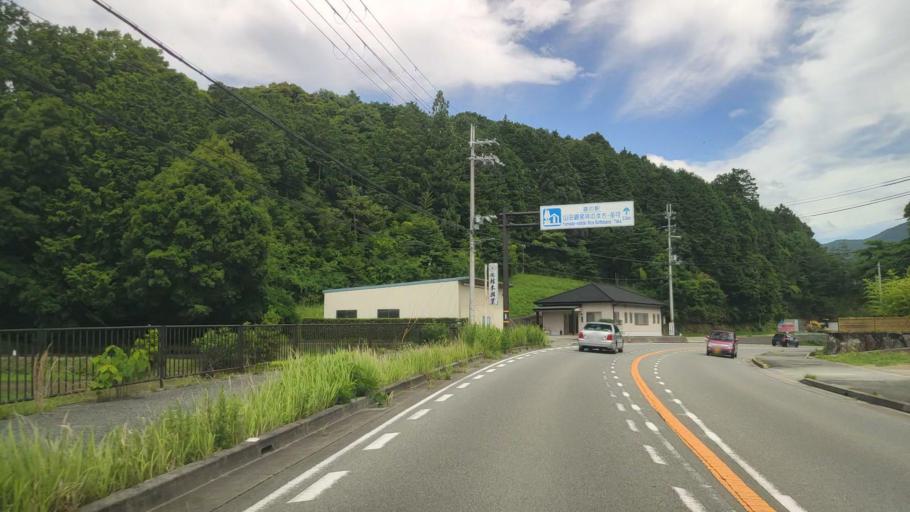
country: JP
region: Hyogo
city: Nishiwaki
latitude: 35.0543
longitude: 134.9172
